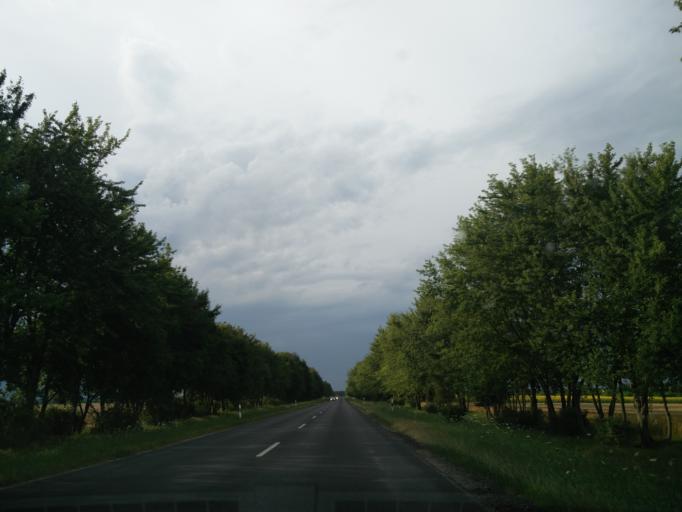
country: HU
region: Vas
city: Vasvar
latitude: 46.9899
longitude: 16.8316
